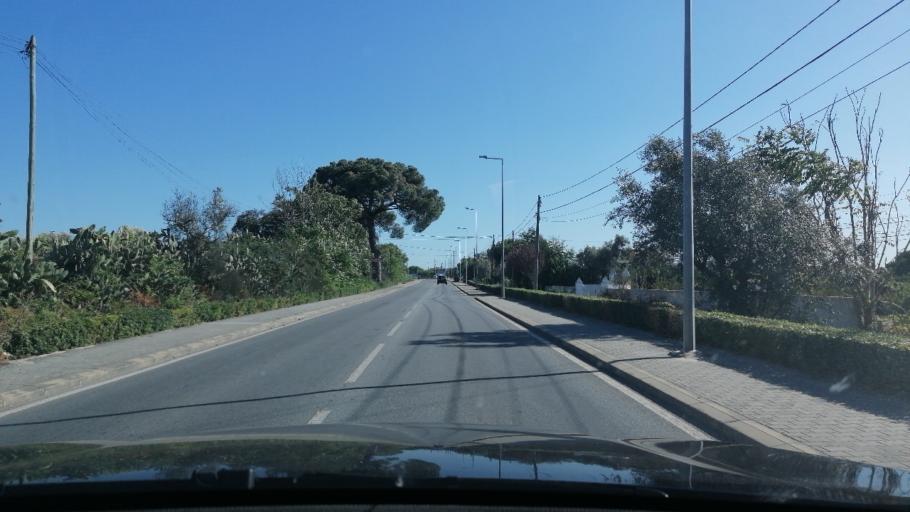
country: PT
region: Setubal
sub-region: Alcacer do Sal
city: Alcacer do Sal
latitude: 38.3841
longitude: -8.5132
